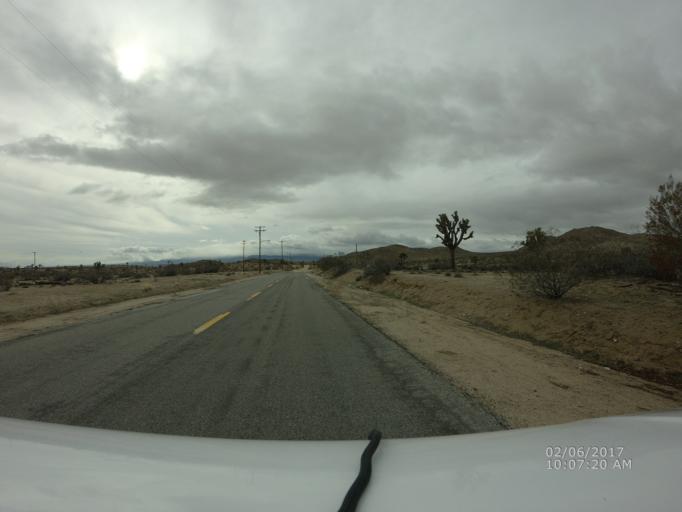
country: US
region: California
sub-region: Los Angeles County
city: Lake Los Angeles
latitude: 34.6914
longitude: -117.7740
